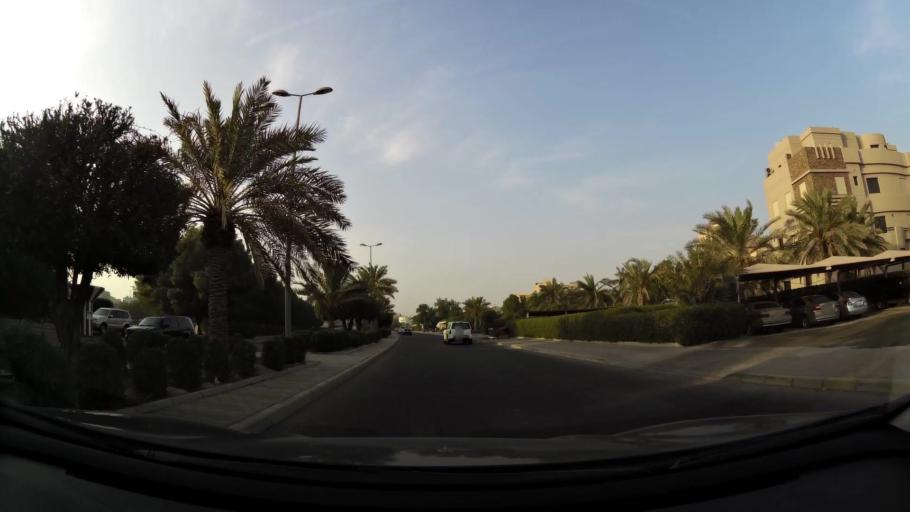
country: KW
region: Mubarak al Kabir
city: Sabah as Salim
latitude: 29.2540
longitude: 48.0710
